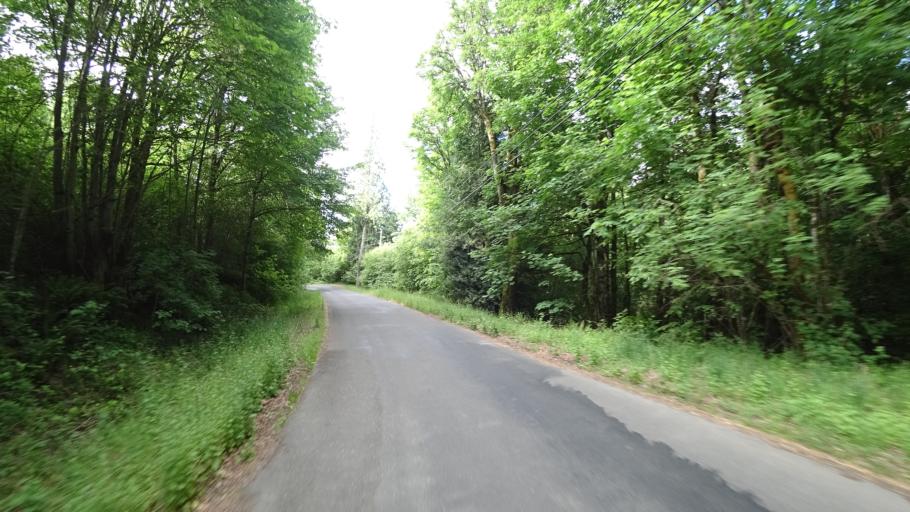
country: US
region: Oregon
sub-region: Washington County
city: Oak Hills
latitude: 45.5803
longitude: -122.8118
